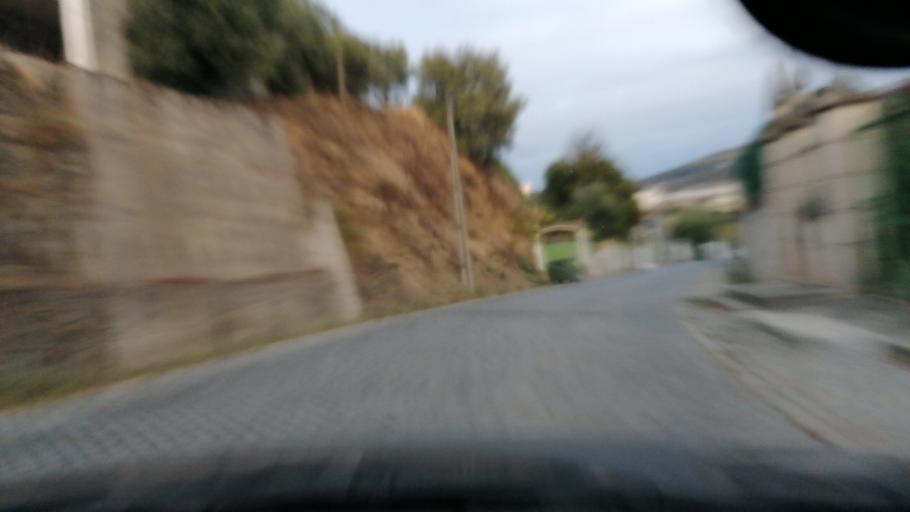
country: PT
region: Vila Real
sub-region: Peso da Regua
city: Peso da Regua
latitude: 41.1615
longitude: -7.7850
